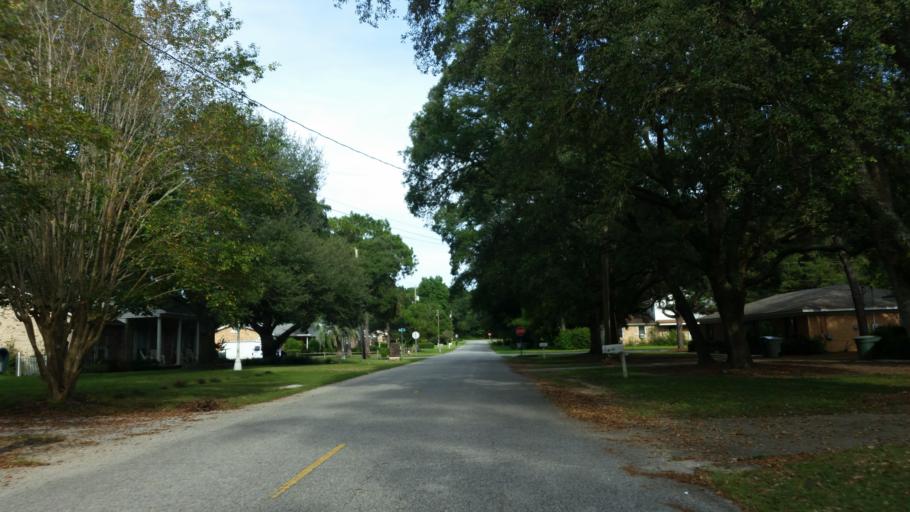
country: US
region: Florida
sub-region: Escambia County
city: Ferry Pass
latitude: 30.5060
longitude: -87.1929
